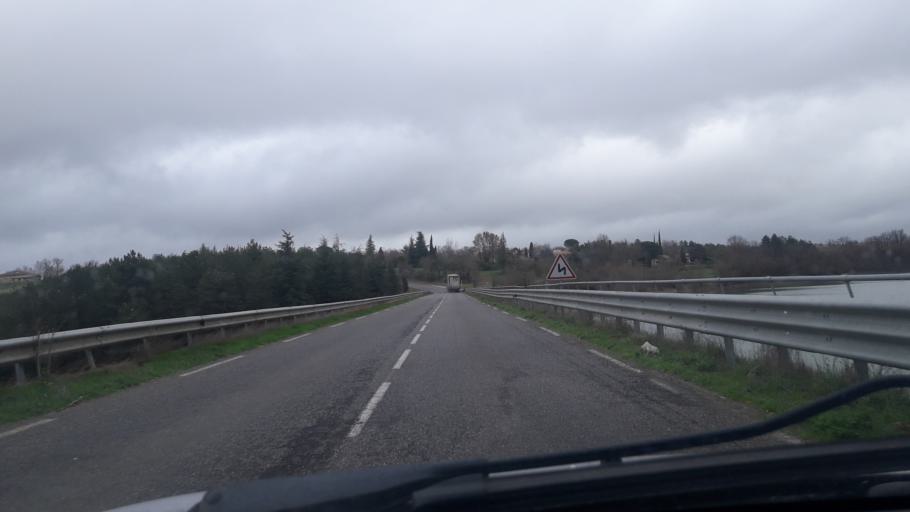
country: FR
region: Midi-Pyrenees
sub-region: Departement du Gers
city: Gimont
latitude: 43.6895
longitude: 0.9983
